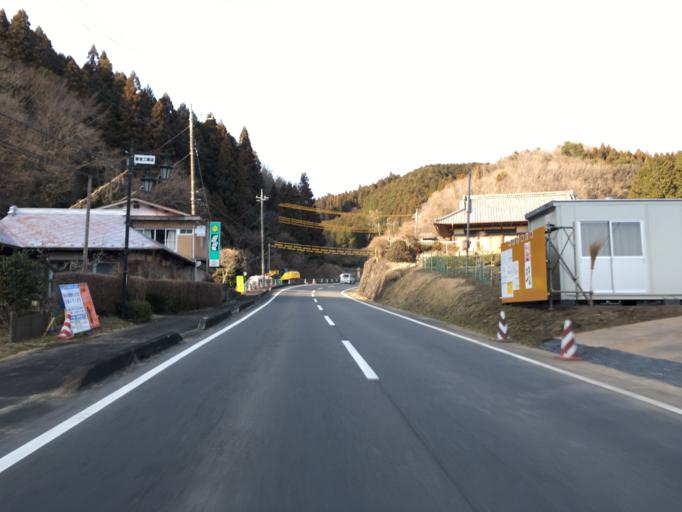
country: JP
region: Ibaraki
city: Daigo
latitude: 36.7449
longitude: 140.4533
